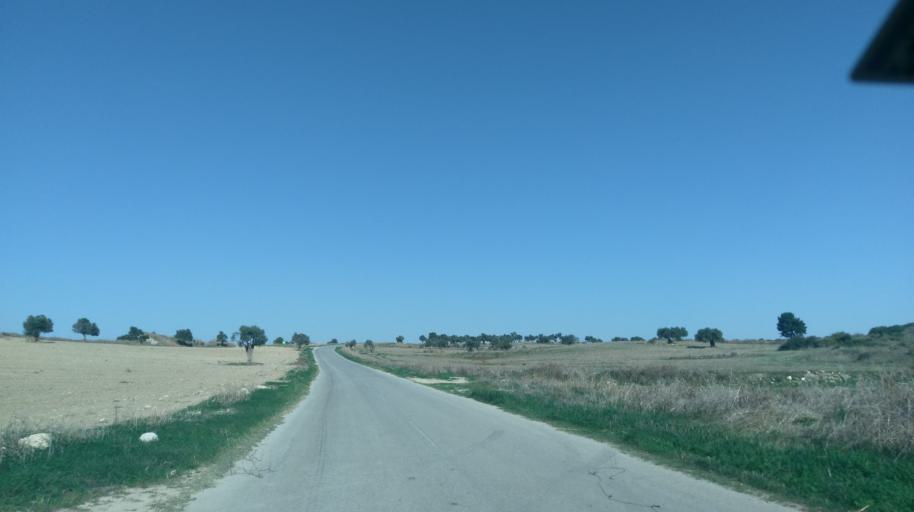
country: CY
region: Ammochostos
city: Trikomo
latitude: 35.3410
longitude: 33.9635
